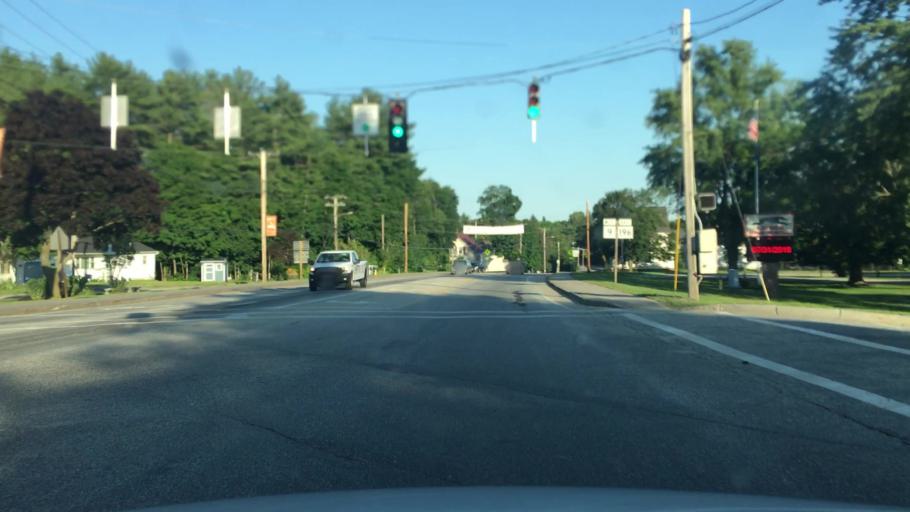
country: US
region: Maine
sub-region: Androscoggin County
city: Lisbon Falls
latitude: 44.0040
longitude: -70.0710
